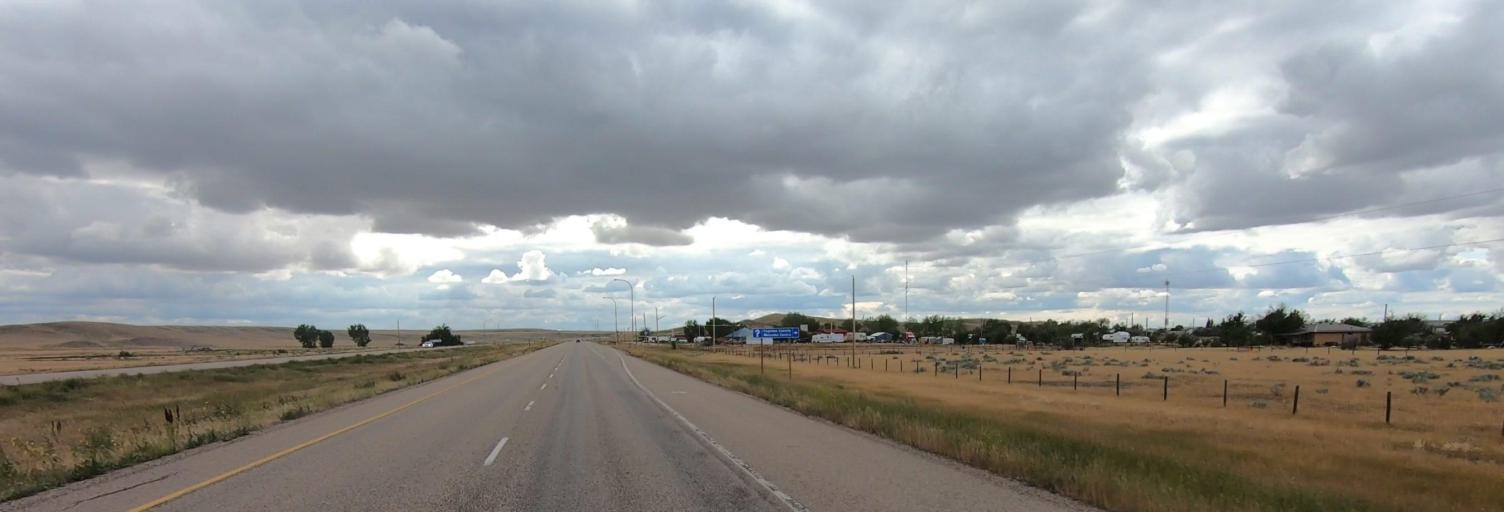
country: CA
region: Saskatchewan
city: Maple Creek
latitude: 49.9448
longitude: -110.0363
